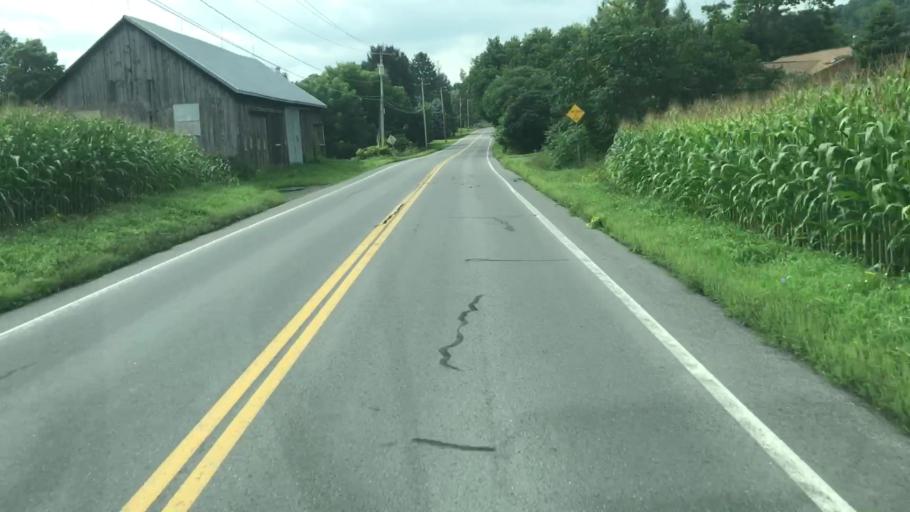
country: US
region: New York
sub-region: Onondaga County
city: Peru
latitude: 43.0597
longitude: -76.3642
